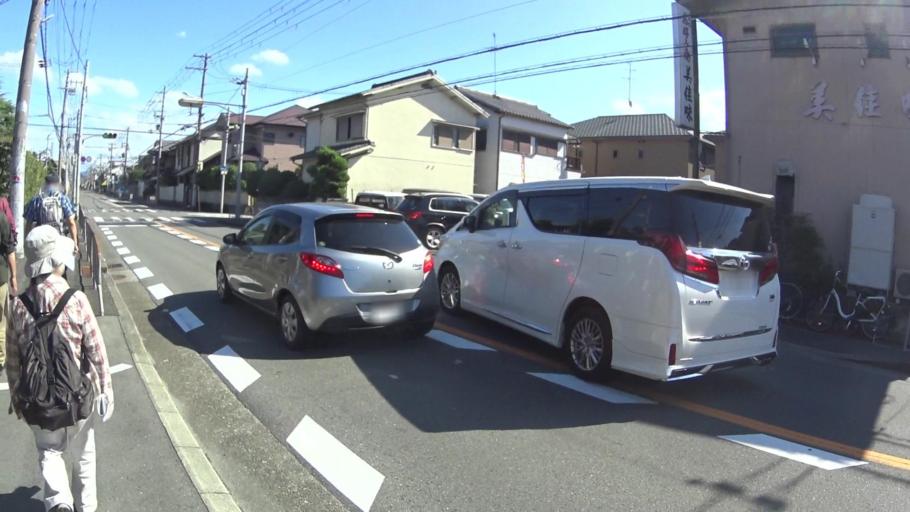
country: JP
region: Ehime
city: Kihoku-cho
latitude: 33.3754
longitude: 132.8088
